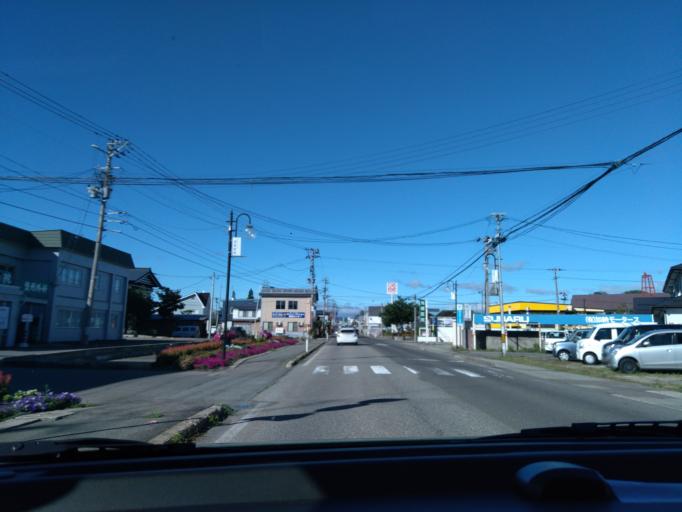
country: JP
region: Akita
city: Yuzawa
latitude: 39.2194
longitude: 140.5202
